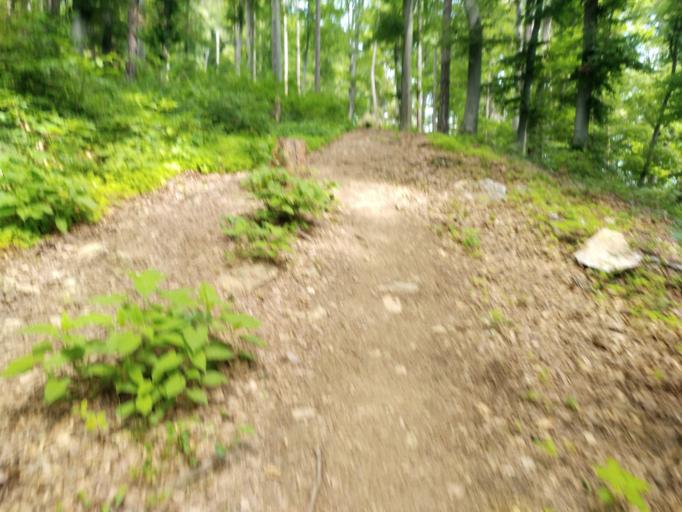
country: AT
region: Styria
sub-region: Graz Stadt
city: Wetzelsdorf
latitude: 47.0363
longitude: 15.3783
